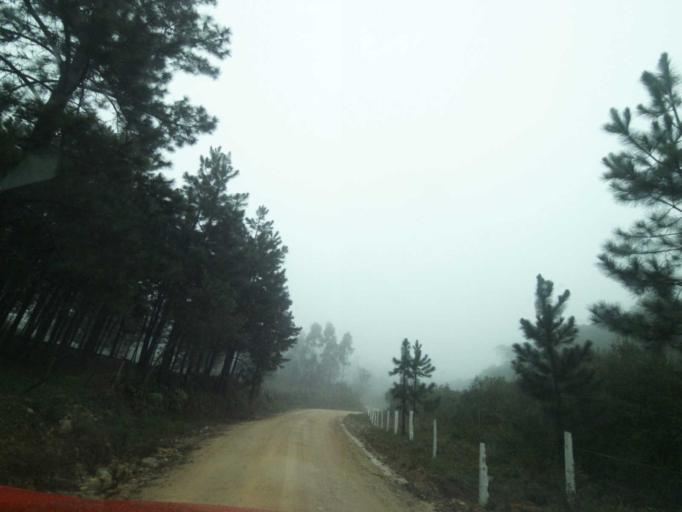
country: BR
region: Santa Catarina
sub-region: Anitapolis
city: Anitapolis
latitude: -27.9045
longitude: -49.1631
